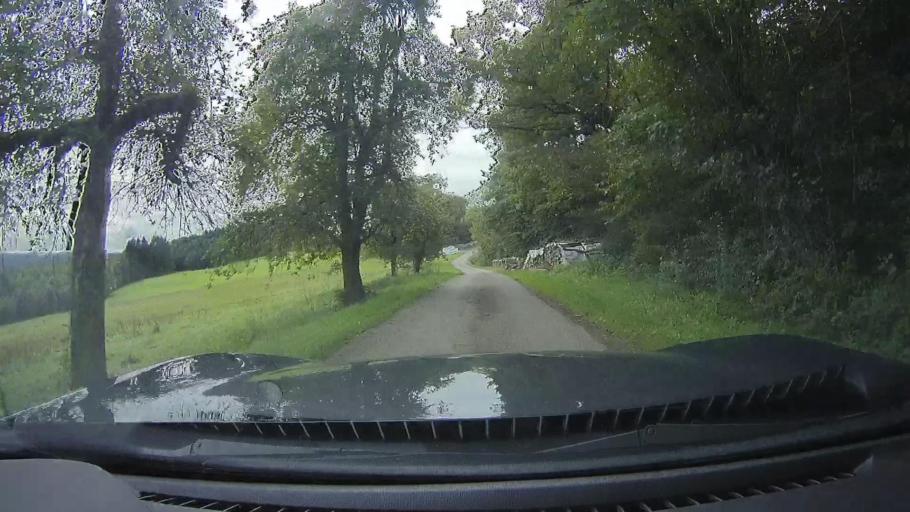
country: DE
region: Baden-Wuerttemberg
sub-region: Regierungsbezirk Stuttgart
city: Wustenrot
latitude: 49.0550
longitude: 9.4721
